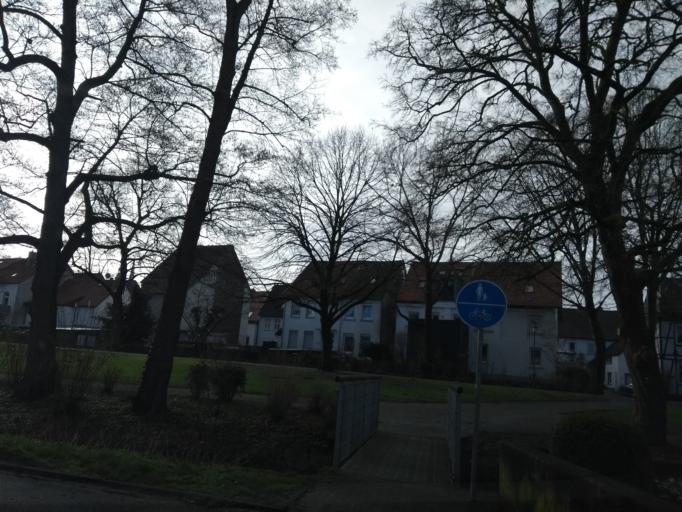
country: DE
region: North Rhine-Westphalia
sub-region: Regierungsbezirk Detmold
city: Lemgo
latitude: 52.0305
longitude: 8.8992
